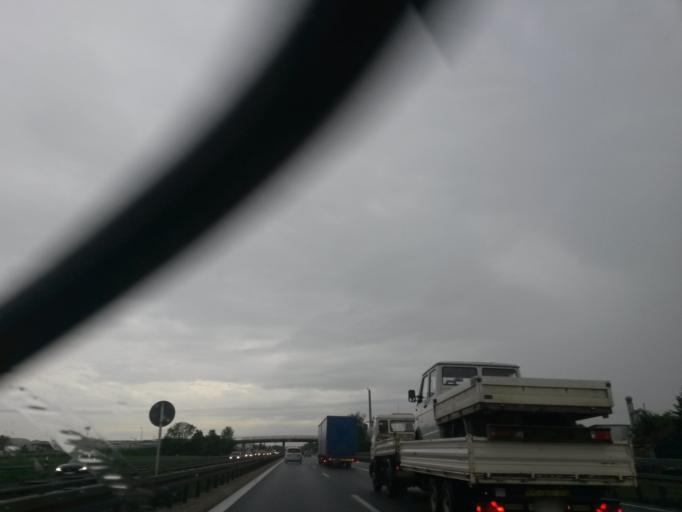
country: DE
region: Bavaria
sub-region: Regierungsbezirk Mittelfranken
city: Baiersdorf
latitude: 49.6704
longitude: 11.0456
